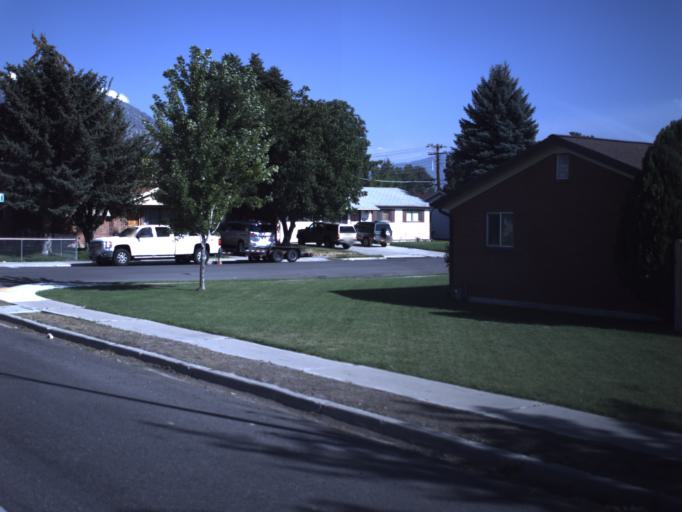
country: US
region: Utah
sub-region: Utah County
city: Provo
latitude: 40.2339
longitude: -111.6922
